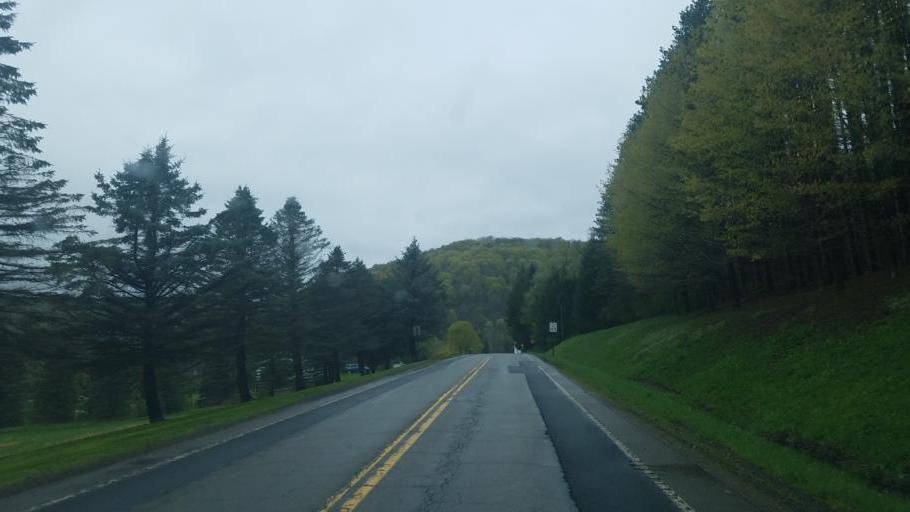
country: US
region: Pennsylvania
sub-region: Potter County
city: Coudersport
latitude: 41.8144
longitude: -78.0029
